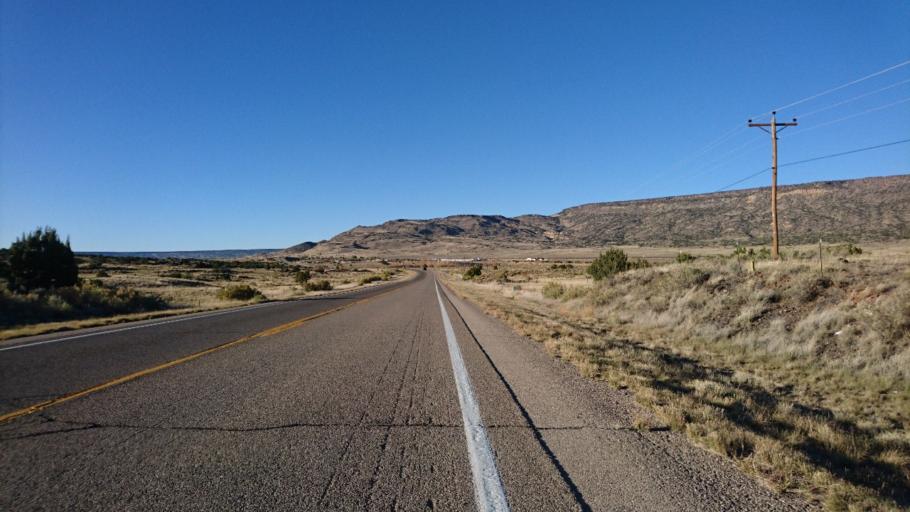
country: US
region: New Mexico
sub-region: Cibola County
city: Grants
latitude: 35.0921
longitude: -107.7710
